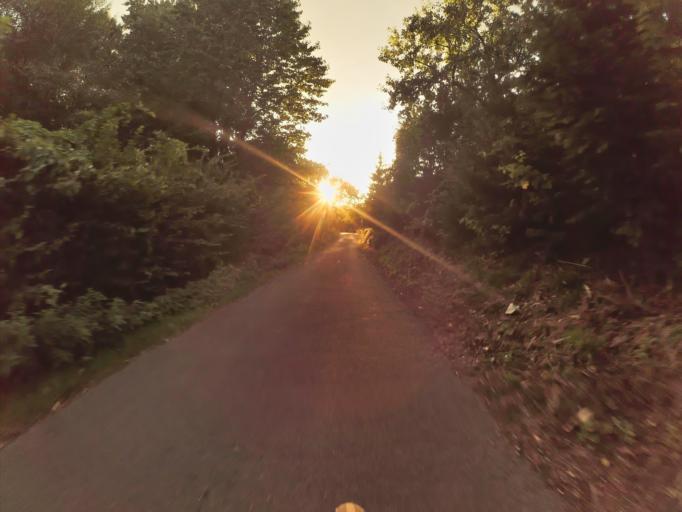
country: DE
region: North Rhine-Westphalia
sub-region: Regierungsbezirk Munster
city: Mettingen
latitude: 52.2774
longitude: 7.7760
